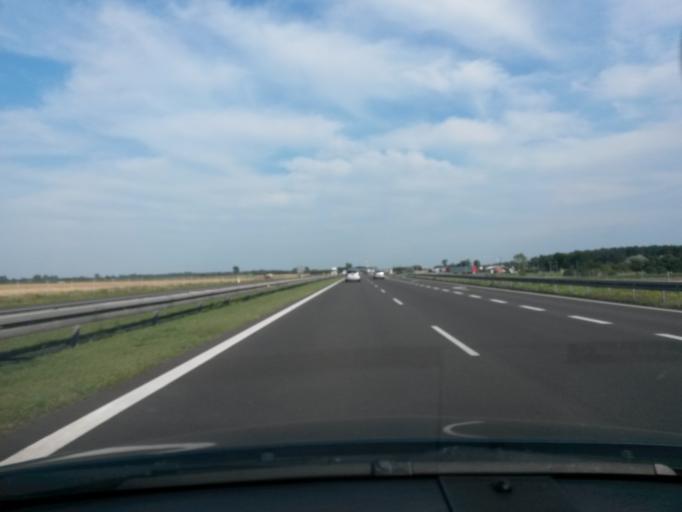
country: PL
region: Greater Poland Voivodeship
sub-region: Powiat slupecki
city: Ladek
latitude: 52.2276
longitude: 17.9262
